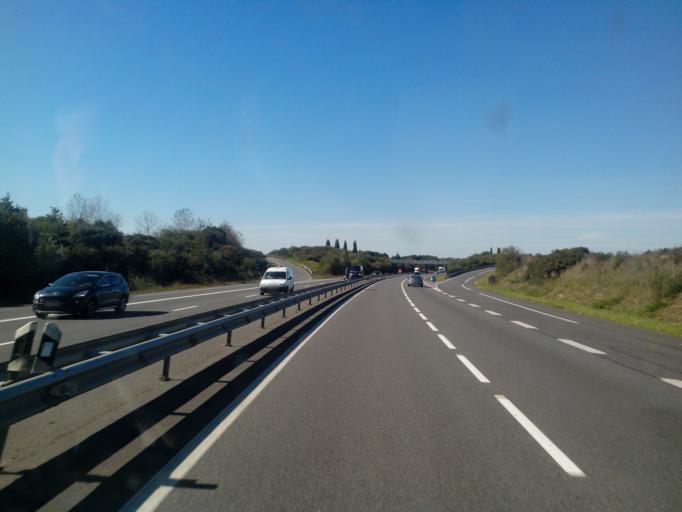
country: FR
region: Pays de la Loire
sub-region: Departement de la Loire-Atlantique
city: Pontchateau
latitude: 47.4211
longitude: -2.0519
